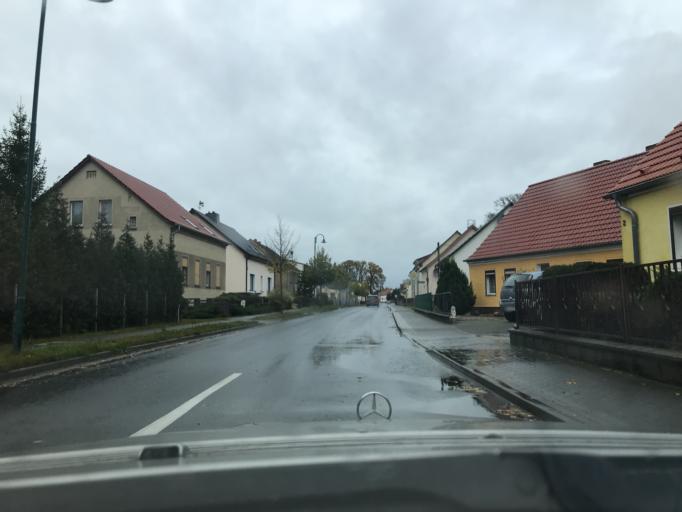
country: DE
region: Brandenburg
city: Trebbin
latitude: 52.2176
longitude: 13.2021
